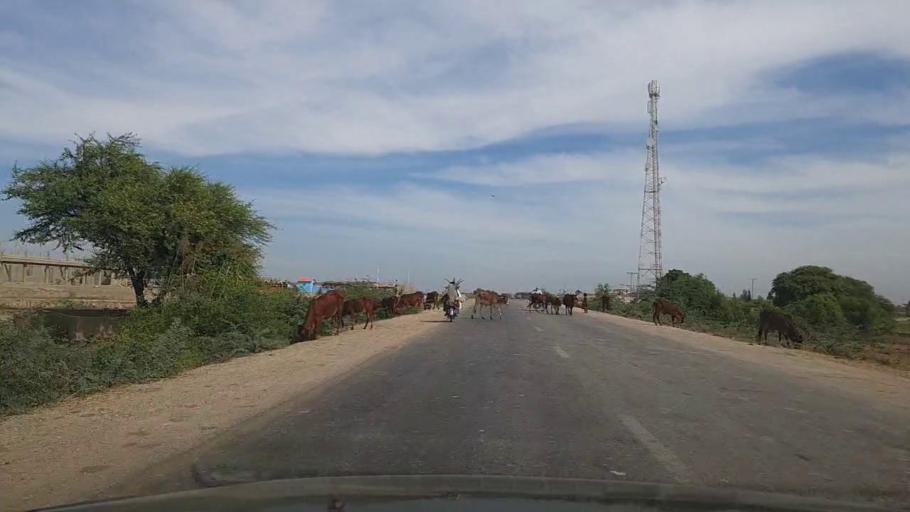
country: PK
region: Sindh
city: Thatta
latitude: 24.8108
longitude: 67.9755
